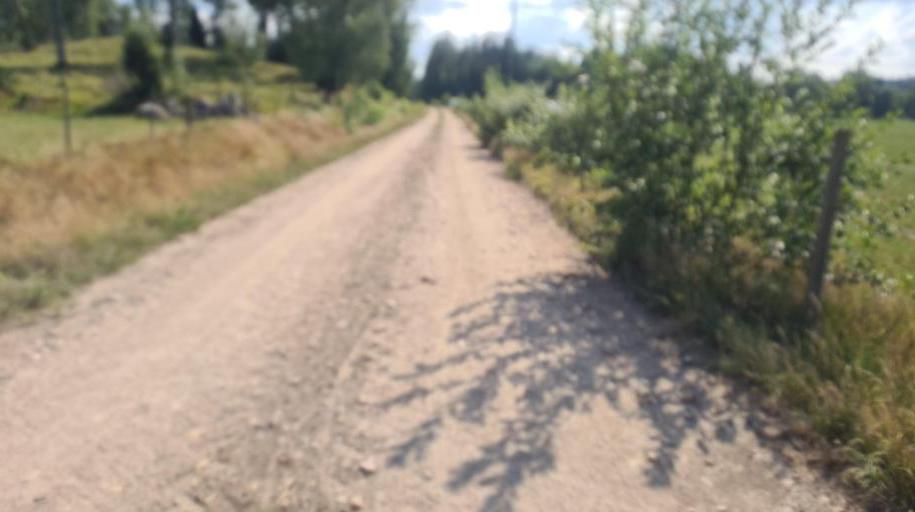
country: SE
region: Kronoberg
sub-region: Ljungby Kommun
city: Ljungby
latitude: 56.7716
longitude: 13.8982
